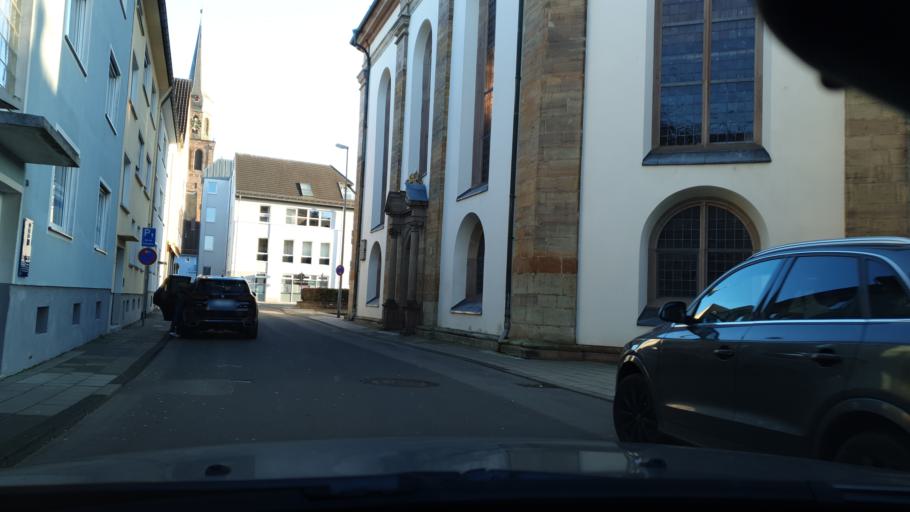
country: DE
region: Rheinland-Pfalz
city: Zweibrucken
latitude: 49.2480
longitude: 7.3621
